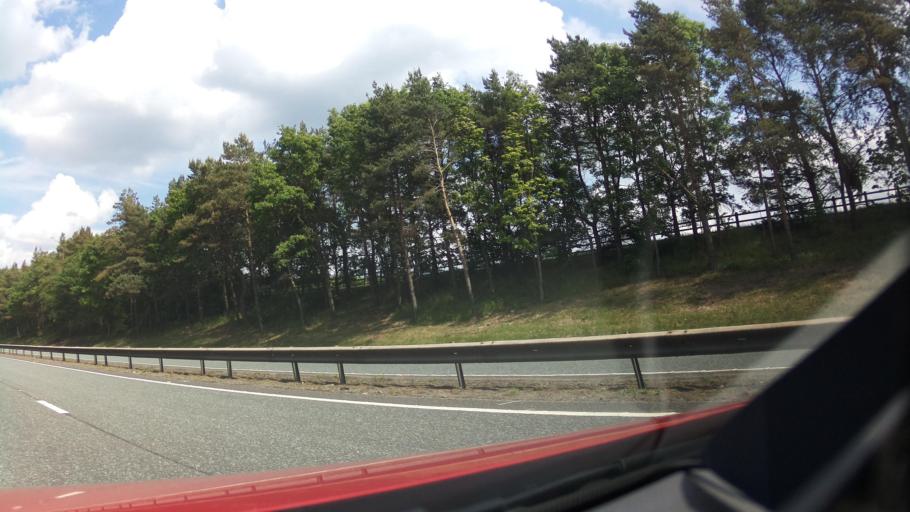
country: GB
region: England
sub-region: Redcar and Cleveland
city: Thornaby-on-Tees
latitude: 54.4861
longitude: -1.3048
